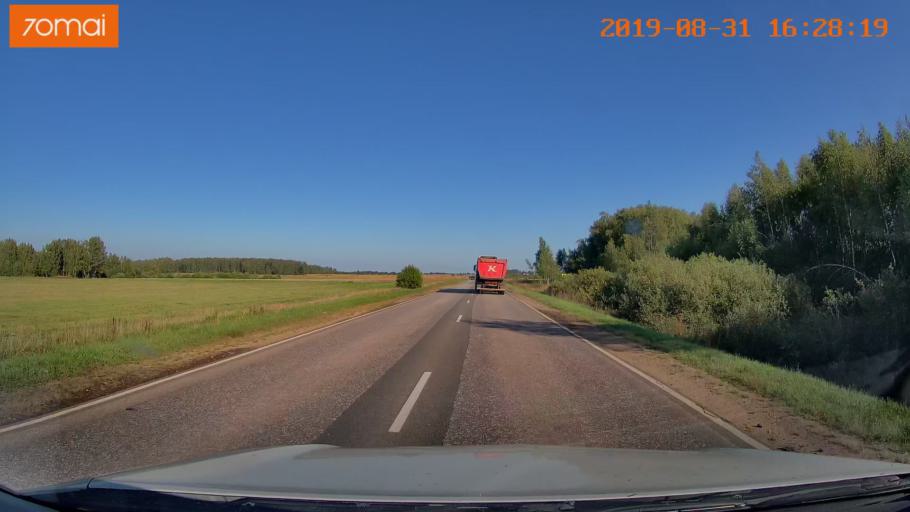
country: RU
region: Kaluga
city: Babynino
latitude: 54.5105
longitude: 35.7766
